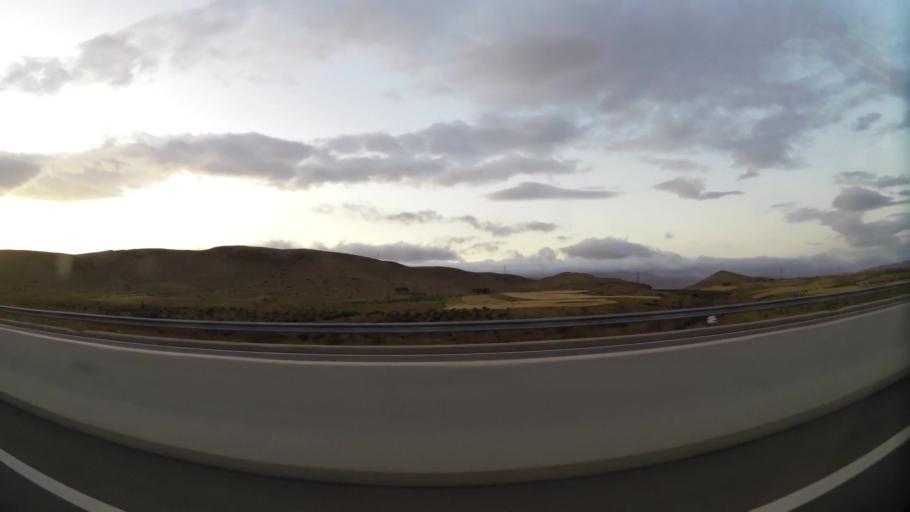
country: MA
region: Oriental
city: El Aioun
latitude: 34.6085
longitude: -2.5679
